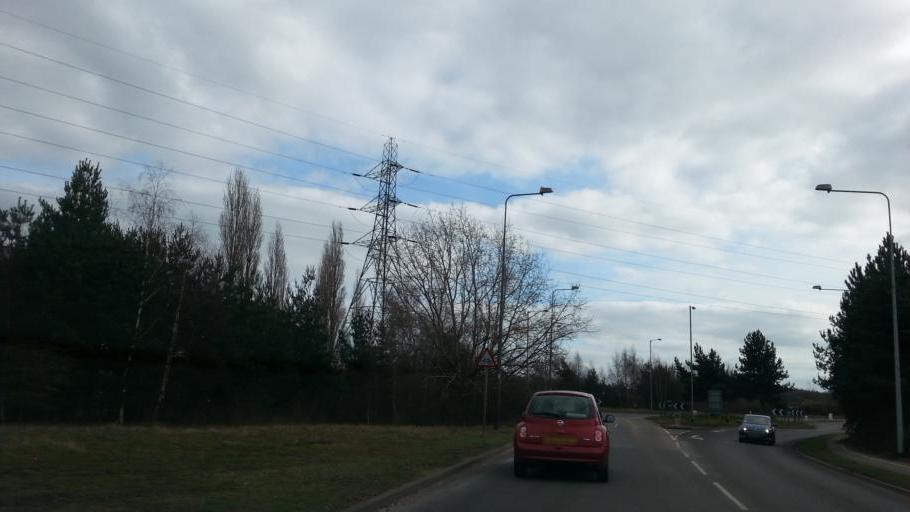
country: GB
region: England
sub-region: Staffordshire
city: Rugeley
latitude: 52.7493
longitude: -1.9118
